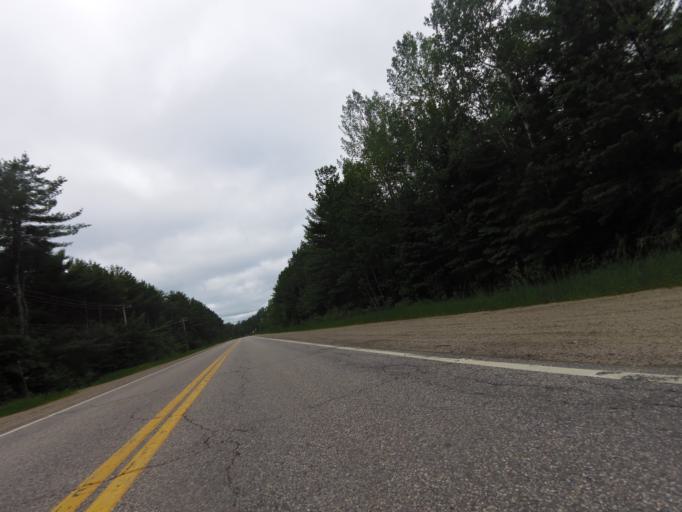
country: CA
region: Quebec
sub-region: Outaouais
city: Shawville
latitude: 45.8582
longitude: -76.4174
